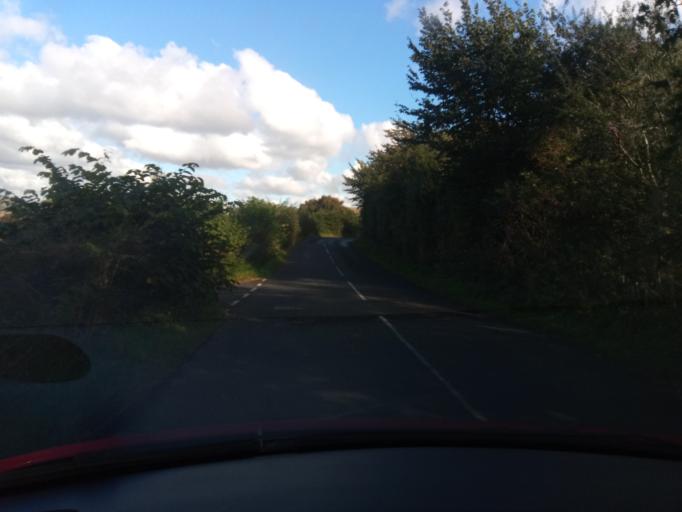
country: GB
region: Scotland
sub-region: The Scottish Borders
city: Coldstream
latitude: 55.5482
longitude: -2.2885
